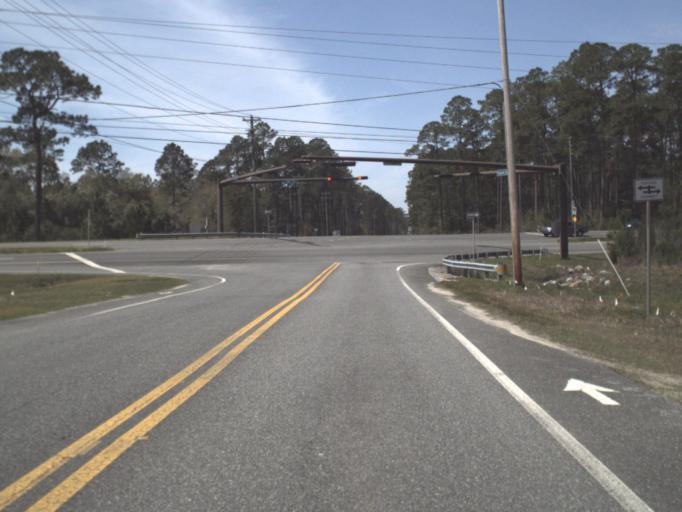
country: US
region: Florida
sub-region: Bay County
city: Lynn Haven
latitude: 30.3222
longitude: -85.6588
